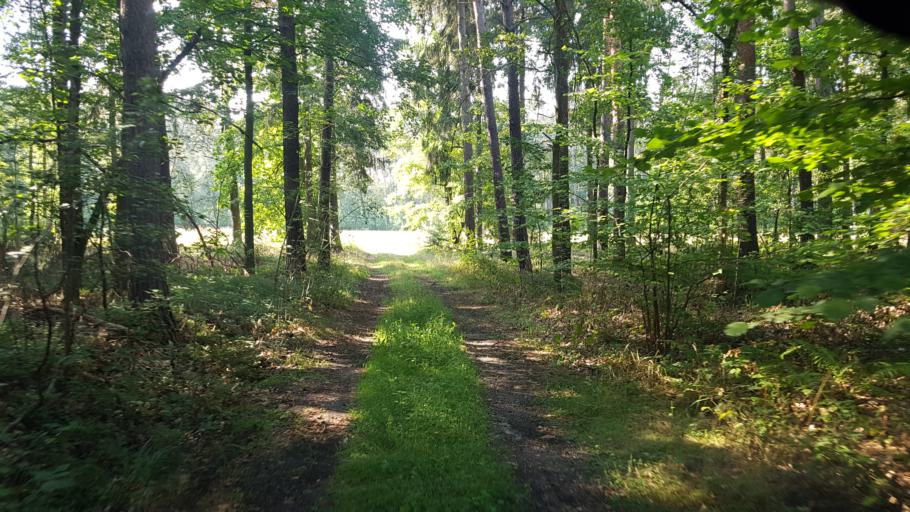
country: DE
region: Brandenburg
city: Finsterwalde
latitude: 51.5933
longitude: 13.6854
